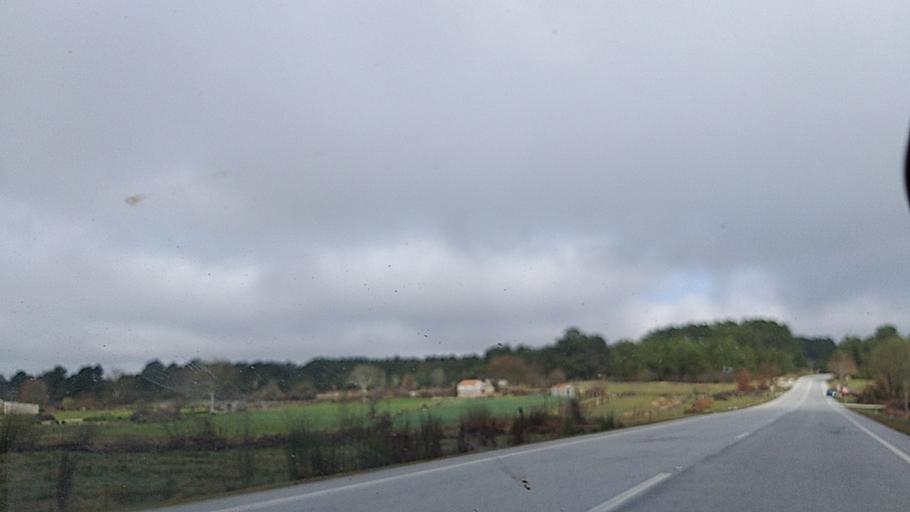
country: PT
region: Guarda
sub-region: Aguiar da Beira
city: Aguiar da Beira
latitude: 40.7461
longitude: -7.5019
